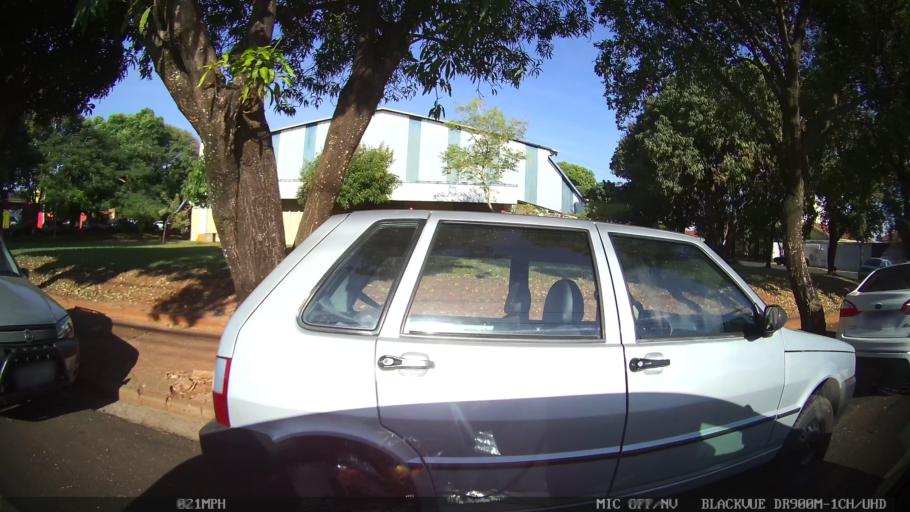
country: BR
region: Sao Paulo
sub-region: Sao Jose Do Rio Preto
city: Sao Jose do Rio Preto
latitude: -20.7953
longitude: -49.3652
